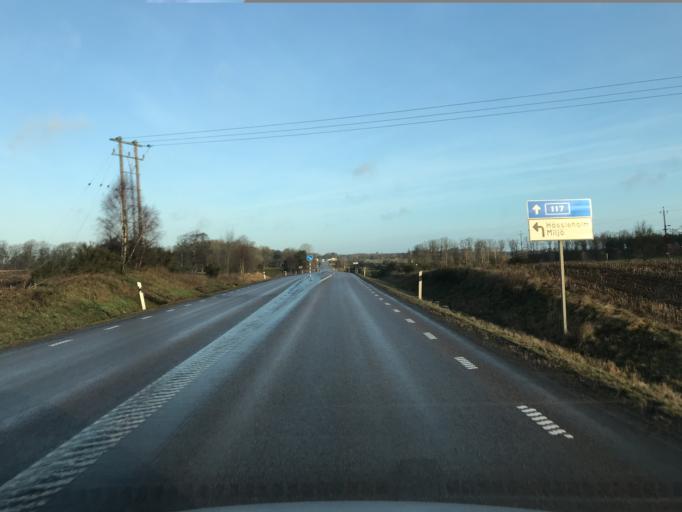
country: SE
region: Skane
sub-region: Hassleholms Kommun
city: Hassleholm
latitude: 56.1857
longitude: 13.7532
